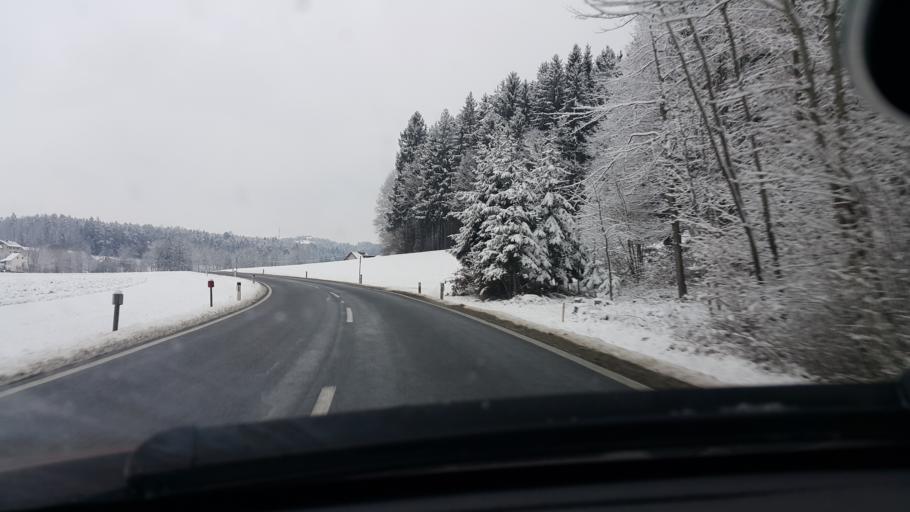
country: AT
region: Styria
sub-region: Politischer Bezirk Graz-Umgebung
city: Hitzendorf
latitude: 47.0501
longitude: 15.2930
